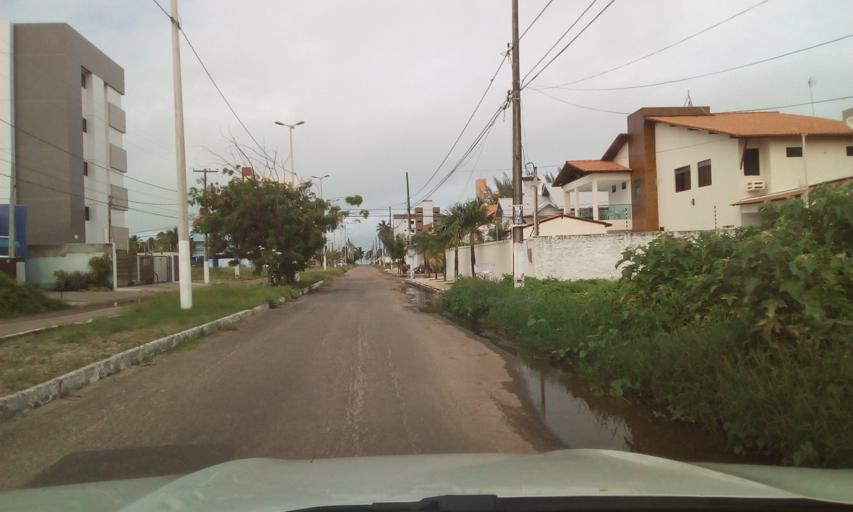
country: BR
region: Paraiba
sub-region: Joao Pessoa
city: Joao Pessoa
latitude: -7.0519
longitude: -34.8464
